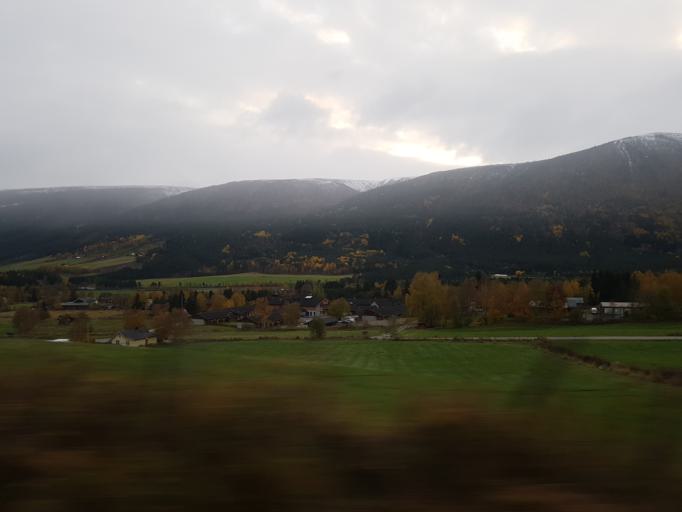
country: NO
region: Oppland
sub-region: Dovre
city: Dovre
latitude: 61.9792
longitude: 9.2482
